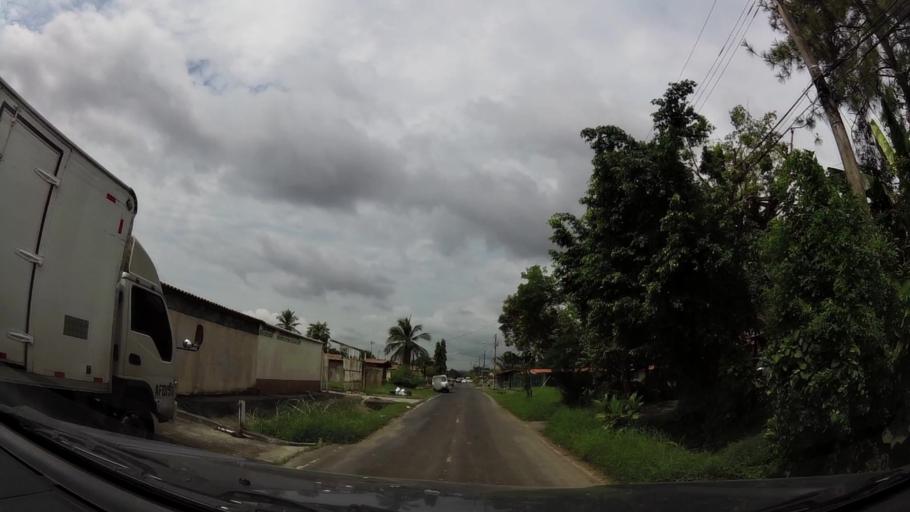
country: PA
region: Panama
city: San Miguelito
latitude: 9.0440
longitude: -79.4214
